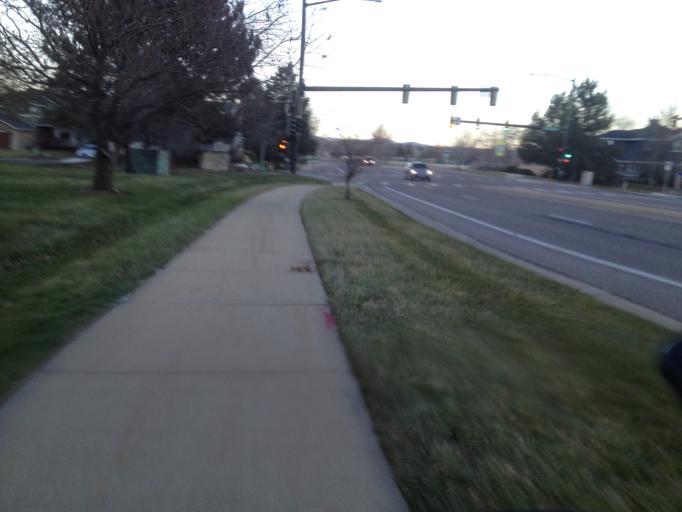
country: US
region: Colorado
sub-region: Boulder County
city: Superior
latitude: 39.9564
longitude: -105.1507
